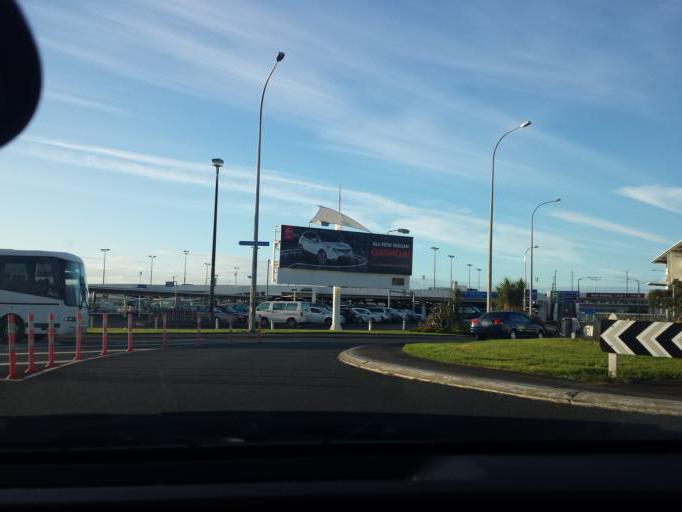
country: NZ
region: Auckland
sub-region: Auckland
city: Mangere
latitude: -37.0044
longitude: 174.7905
